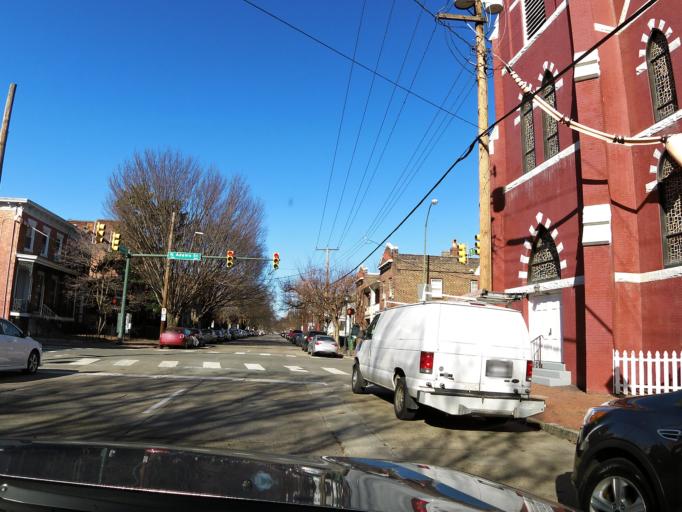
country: US
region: Virginia
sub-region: City of Richmond
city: Richmond
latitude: 37.5478
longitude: -77.4410
